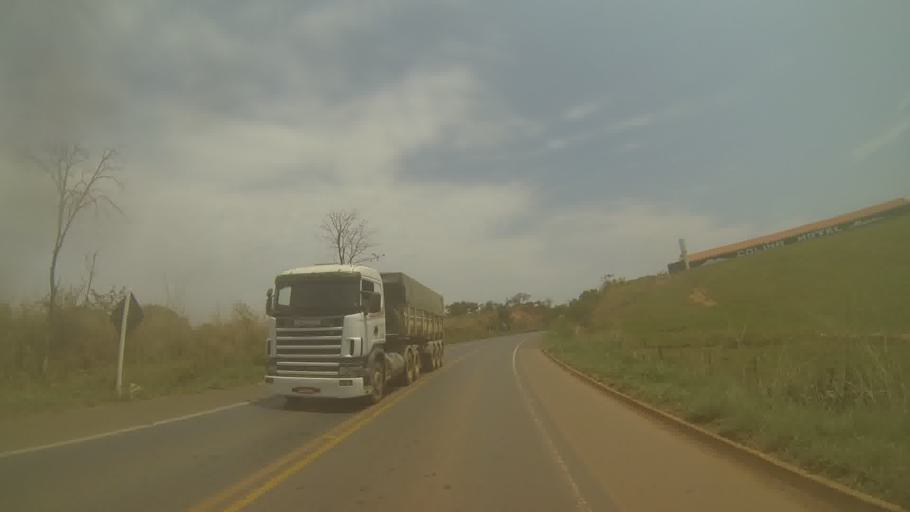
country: BR
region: Minas Gerais
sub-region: Bambui
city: Bambui
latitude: -20.0158
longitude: -45.9405
